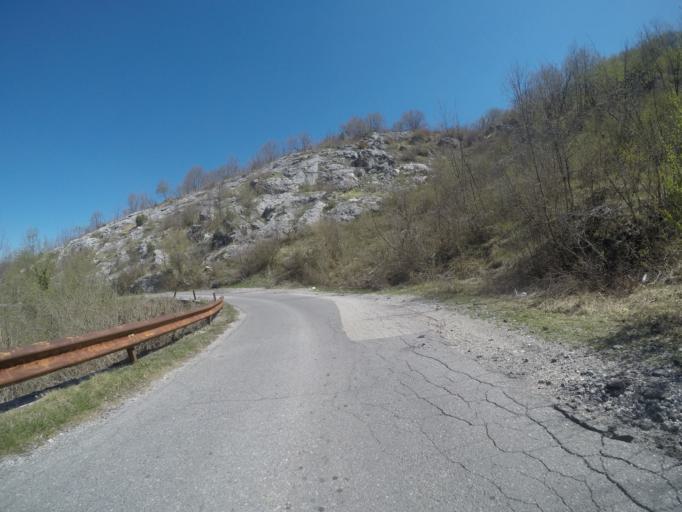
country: ME
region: Cetinje
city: Cetinje
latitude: 42.4447
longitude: 18.8738
